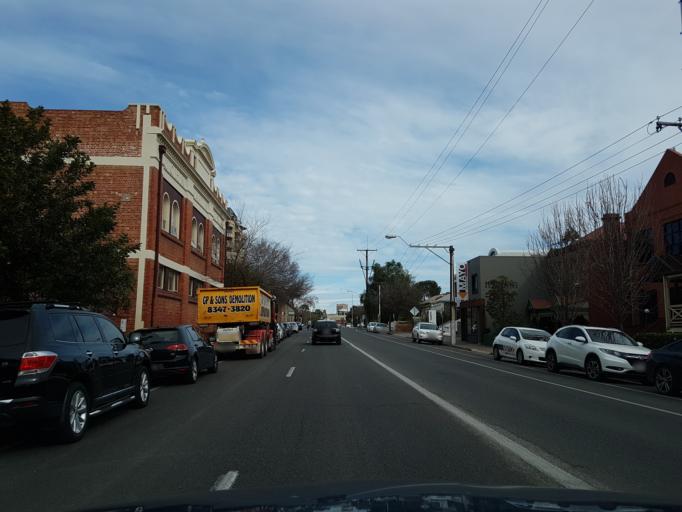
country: AU
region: South Australia
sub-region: Adelaide
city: Adelaide
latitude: -34.9210
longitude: 138.6173
